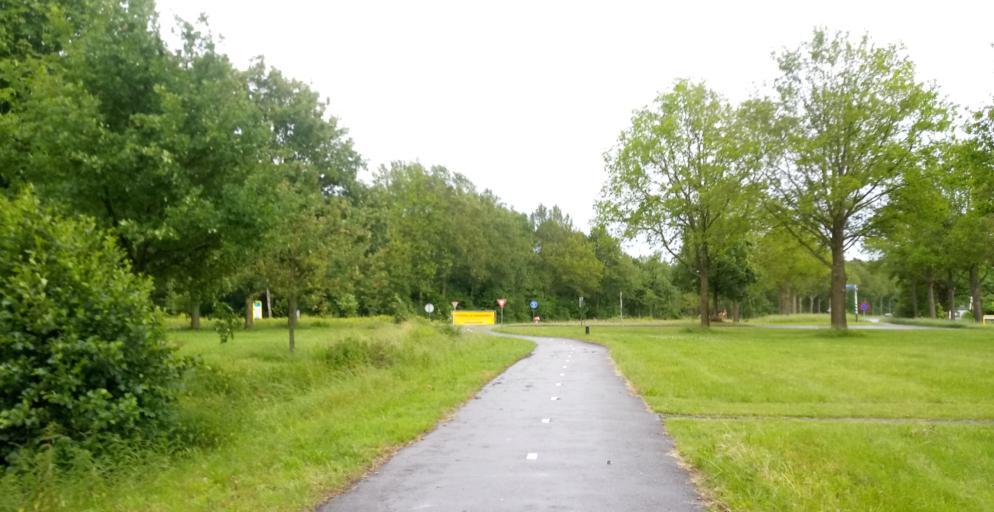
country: NL
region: Gelderland
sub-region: Gemeente Voorst
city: Twello
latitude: 52.2013
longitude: 6.0887
